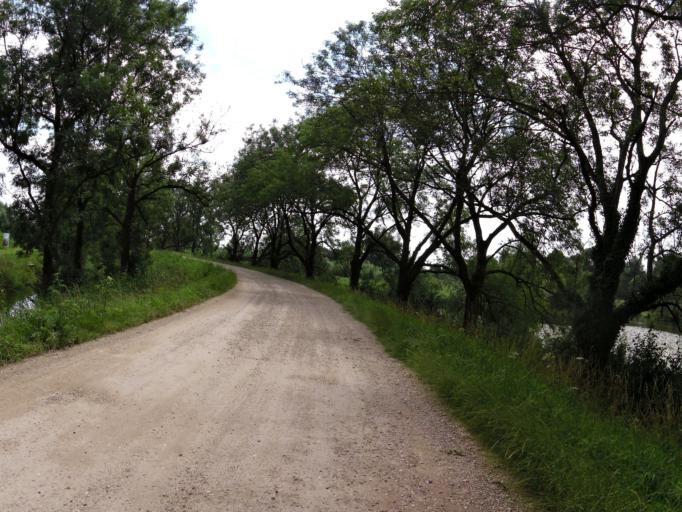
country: NL
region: South Holland
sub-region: Gemeente Leerdam
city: Leerdam
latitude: 51.8771
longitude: 5.1199
